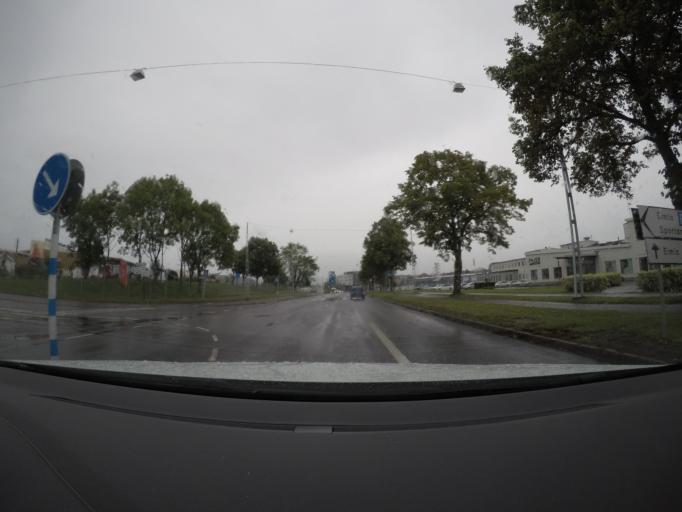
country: SE
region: Joenkoeping
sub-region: Jonkopings Kommun
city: Jonkoping
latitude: 57.7850
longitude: 14.2280
